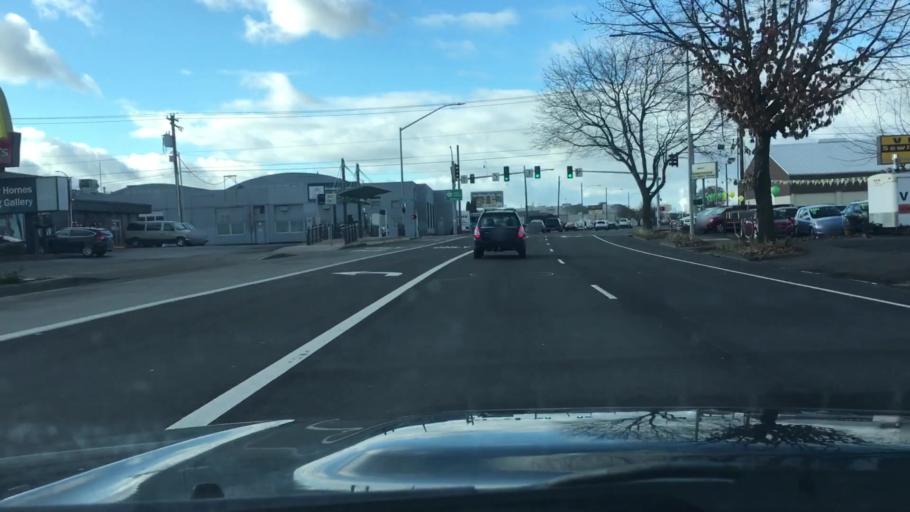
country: US
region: Oregon
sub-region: Lane County
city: Eugene
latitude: 44.0533
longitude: -123.1217
